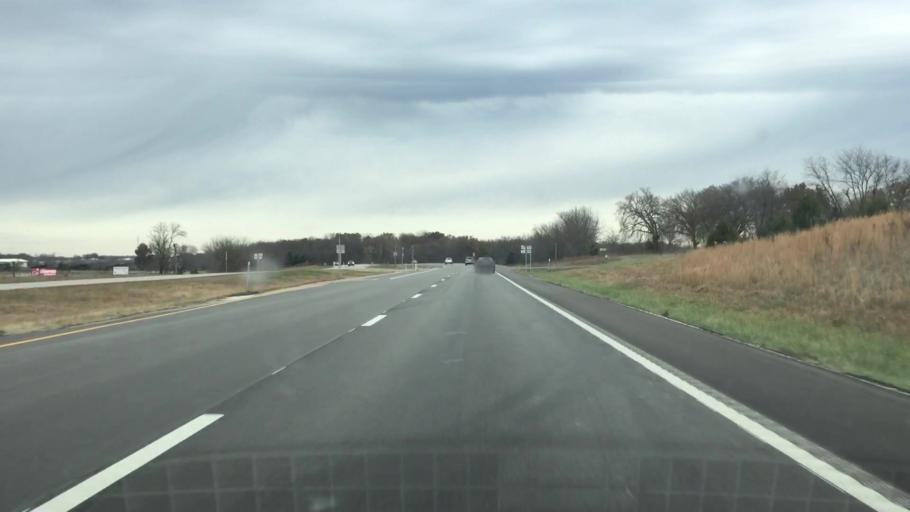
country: US
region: Missouri
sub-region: Saint Clair County
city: Osceola
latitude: 38.0088
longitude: -93.6572
